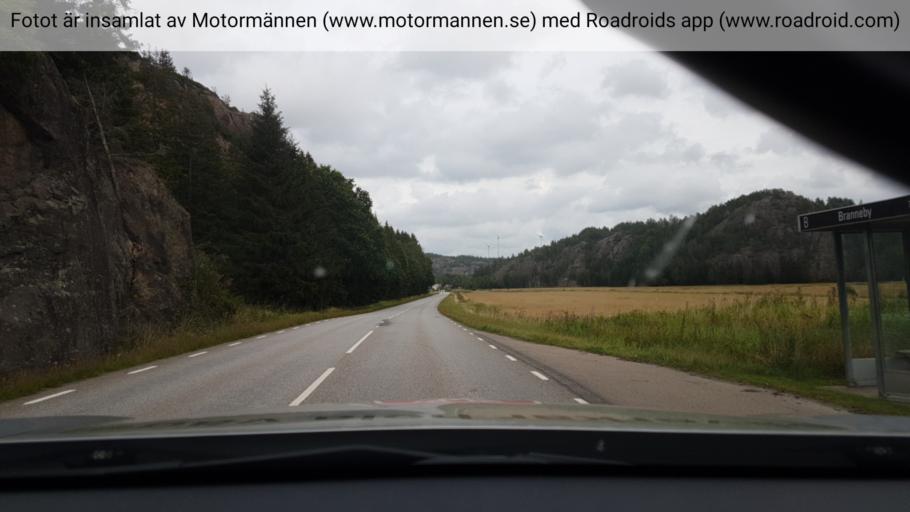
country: SE
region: Vaestra Goetaland
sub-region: Lysekils Kommun
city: Brastad
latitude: 58.5569
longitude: 11.4596
